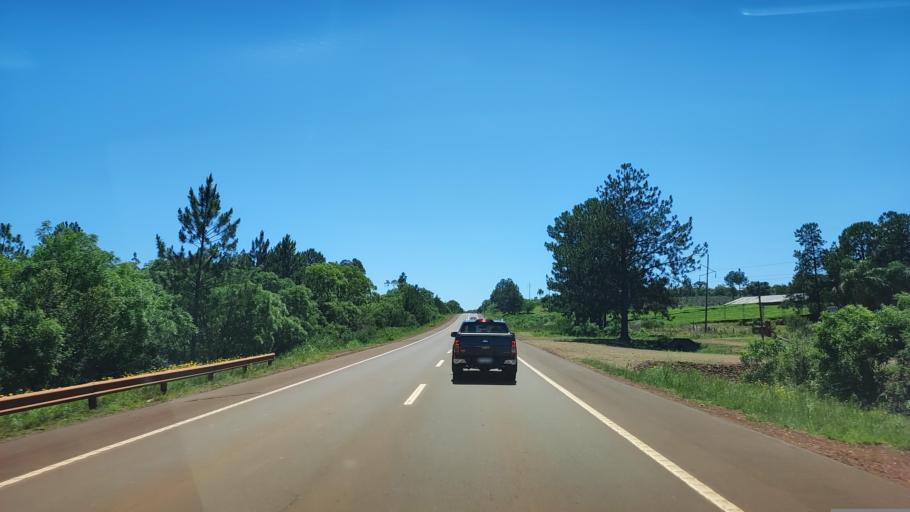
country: AR
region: Misiones
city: Aristobulo del Valle
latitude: -27.0868
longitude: -54.7839
